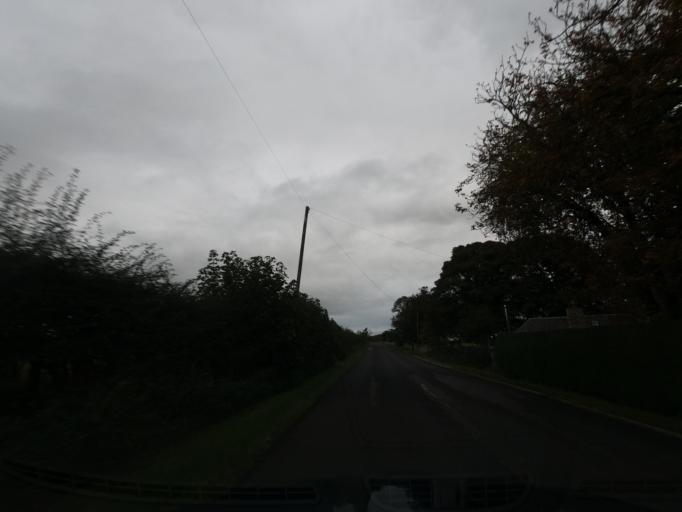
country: GB
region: England
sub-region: Northumberland
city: Ford
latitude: 55.6859
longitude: -2.0871
